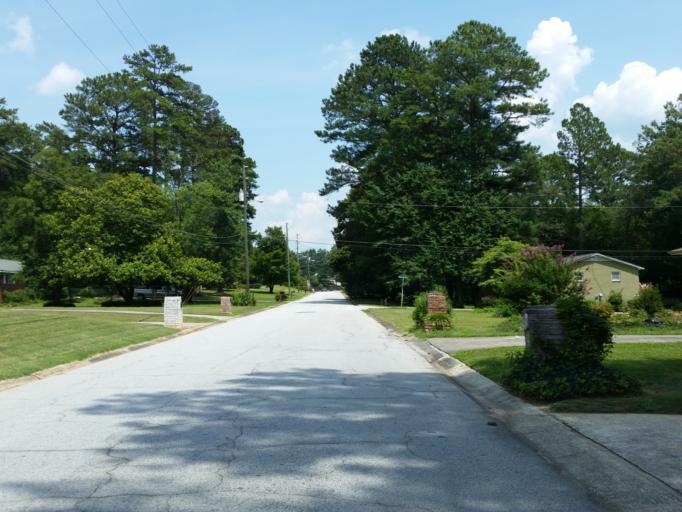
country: US
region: Georgia
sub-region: Cobb County
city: Vinings
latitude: 33.9365
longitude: -84.4640
